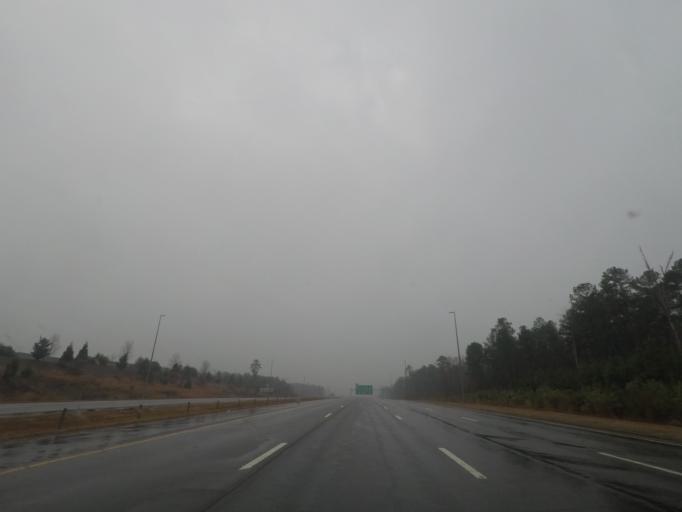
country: US
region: North Carolina
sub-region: Wake County
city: Morrisville
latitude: 35.8648
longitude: -78.8647
